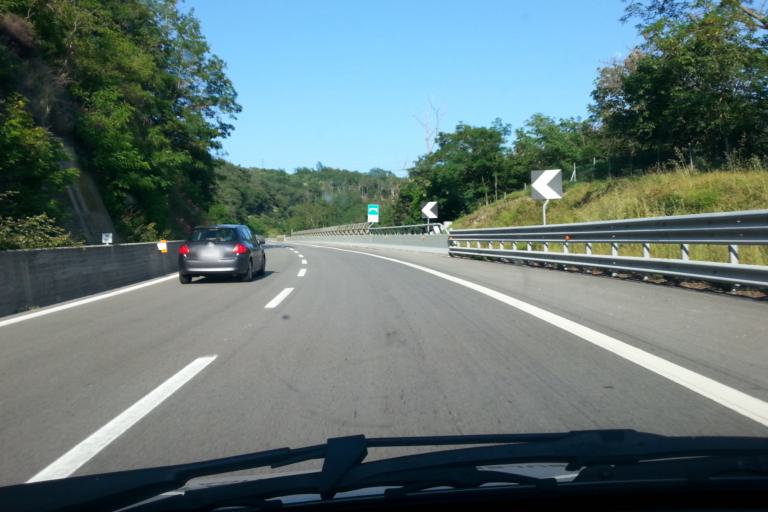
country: IT
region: Liguria
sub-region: Provincia di Savona
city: Quiliano
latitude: 44.2988
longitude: 8.4167
